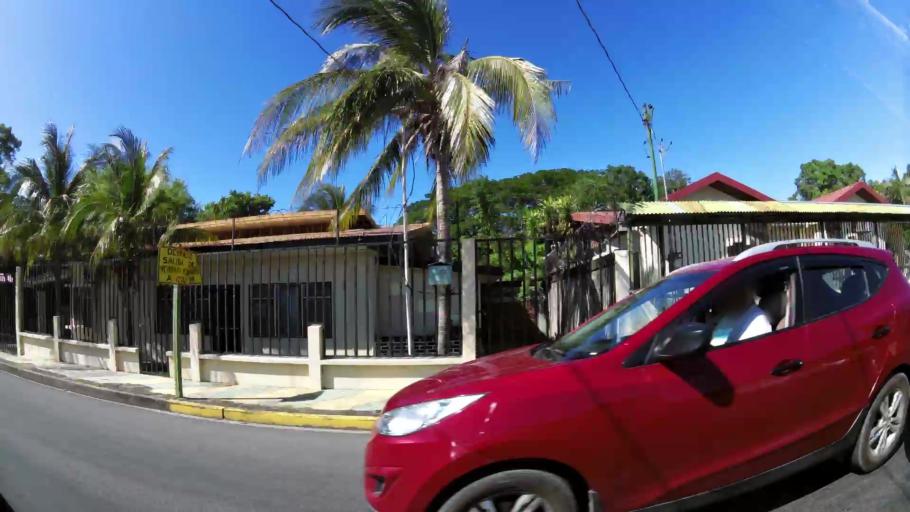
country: CR
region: Guanacaste
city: Liberia
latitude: 10.6339
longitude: -85.4405
